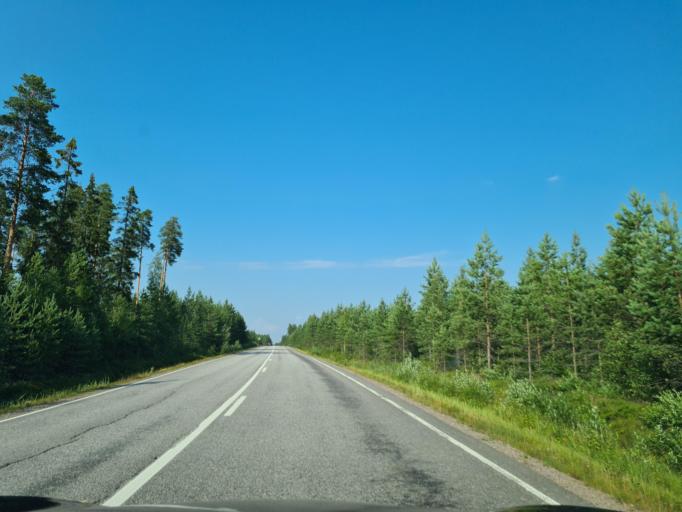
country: FI
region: Satakunta
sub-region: Pohjois-Satakunta
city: Karvia
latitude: 62.2938
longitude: 22.6207
